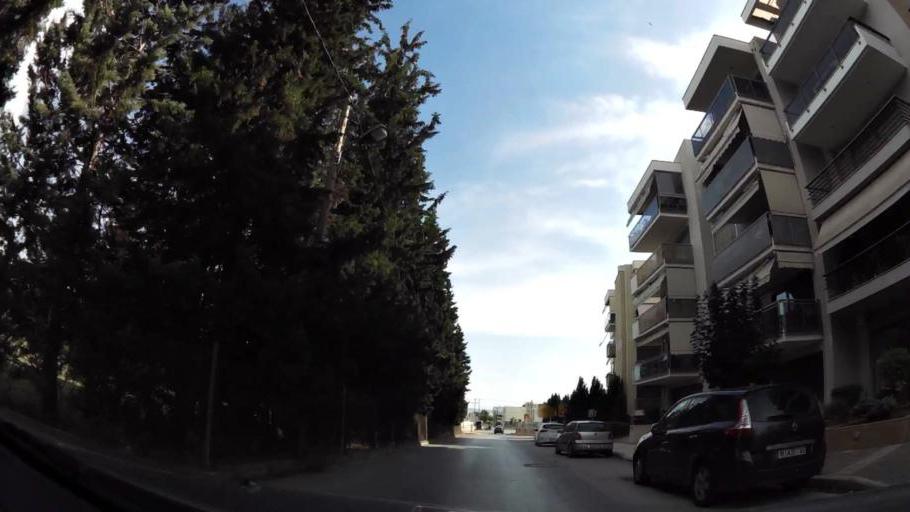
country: GR
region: Central Macedonia
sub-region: Nomos Thessalonikis
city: Kalamaria
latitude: 40.5667
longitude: 22.9689
